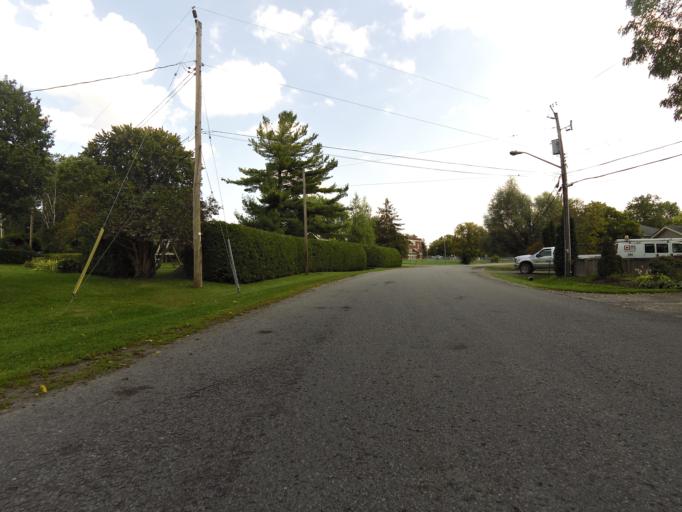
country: CA
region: Ontario
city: Bells Corners
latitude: 45.2297
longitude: -75.6848
